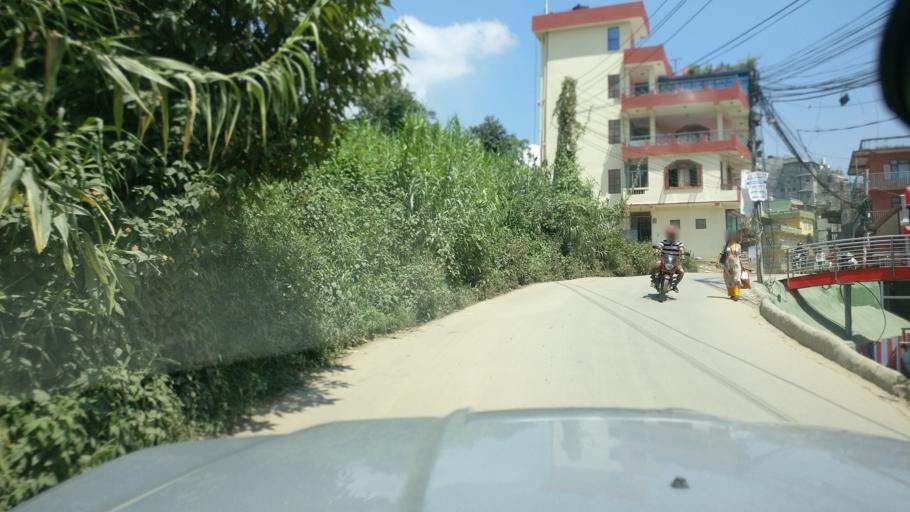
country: NP
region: Central Region
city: Kirtipur
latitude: 27.6939
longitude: 85.2758
